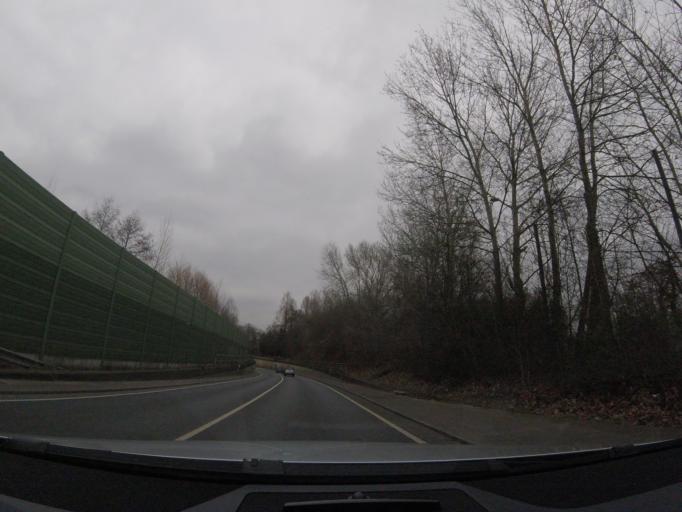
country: DE
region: Hesse
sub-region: Regierungsbezirk Darmstadt
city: Darmstadt
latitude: 49.8718
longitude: 8.6762
